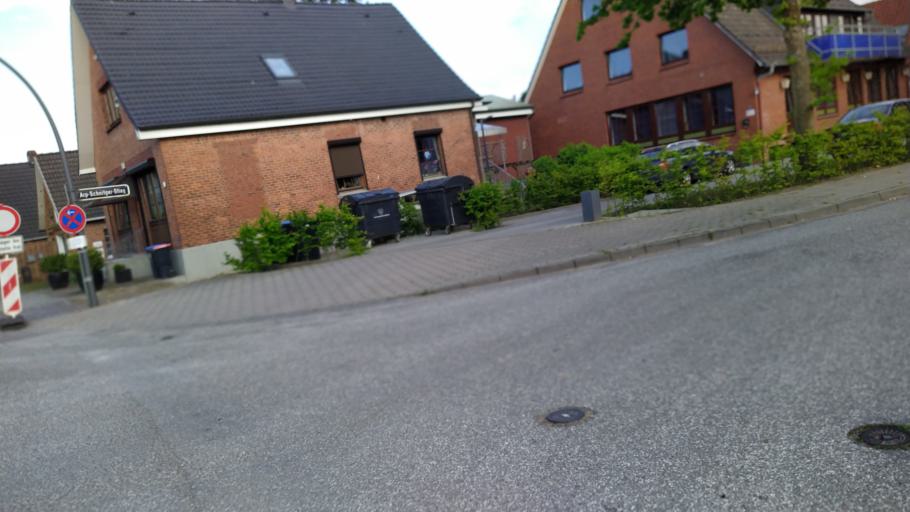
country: DE
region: Lower Saxony
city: Neu Wulmstorf
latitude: 53.5211
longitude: 9.8116
